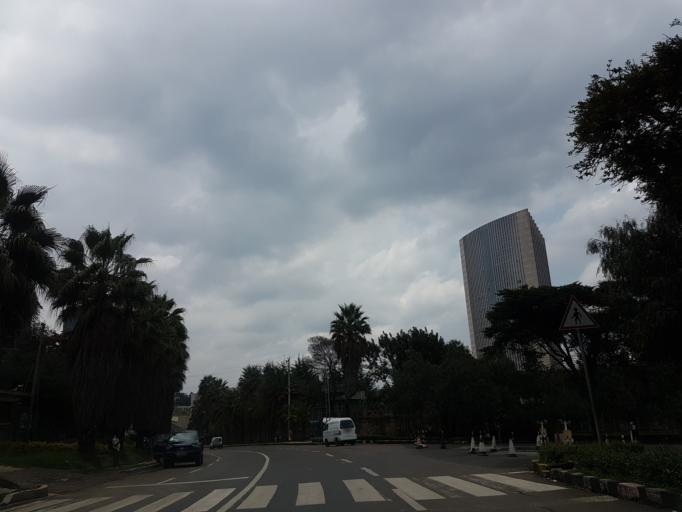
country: ET
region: Adis Abeba
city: Addis Ababa
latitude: 9.0024
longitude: 38.7417
